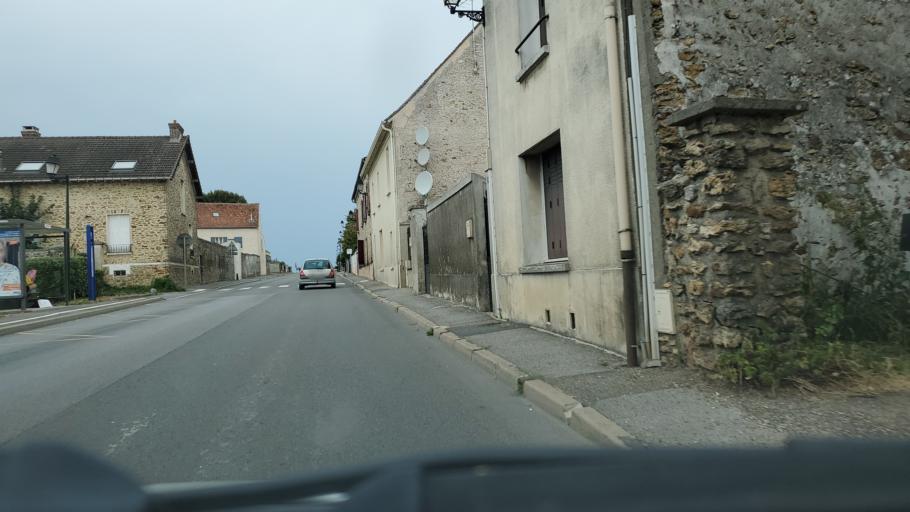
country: FR
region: Ile-de-France
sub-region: Departement de Seine-et-Marne
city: Chailly-en-Brie
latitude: 48.7898
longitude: 3.1233
